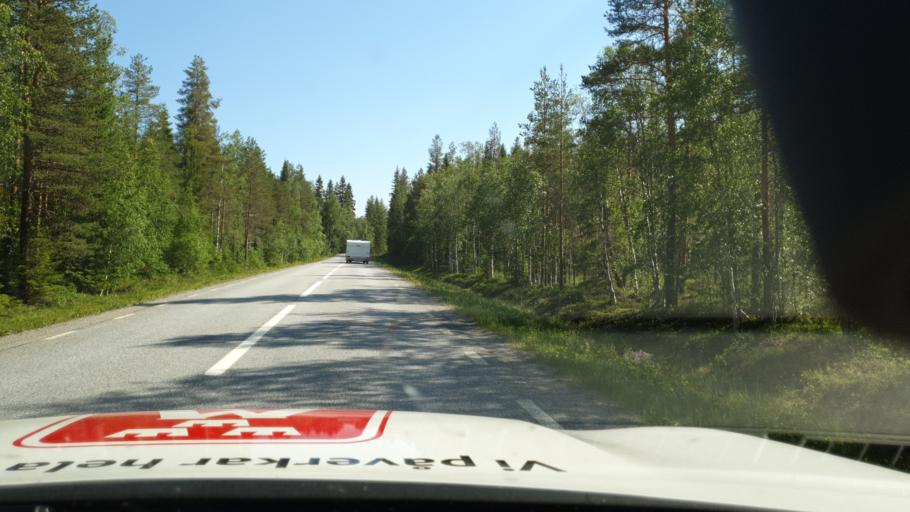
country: SE
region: Vaesterbotten
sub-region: Skelleftea Kommun
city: Burtraesk
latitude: 64.3381
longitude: 20.2330
